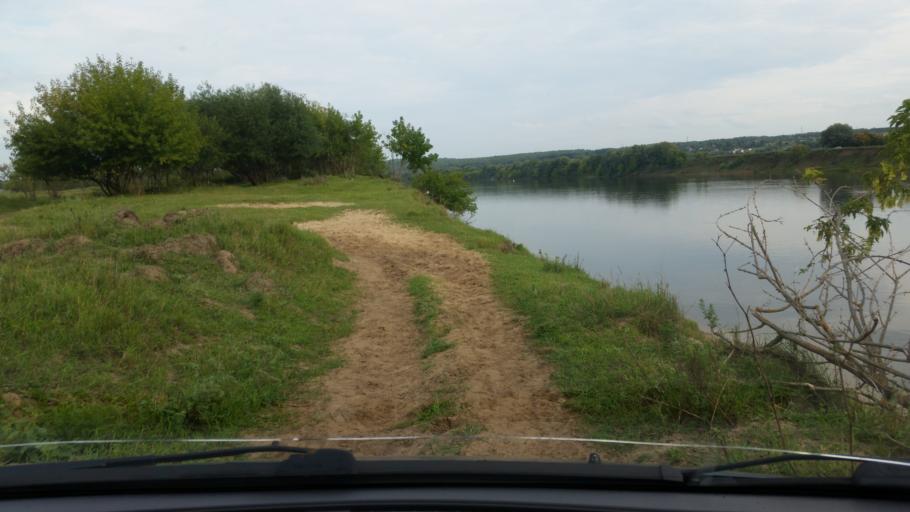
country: RU
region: Moskovskaya
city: Bol'shoye Gryzlovo
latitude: 54.8463
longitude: 37.7082
